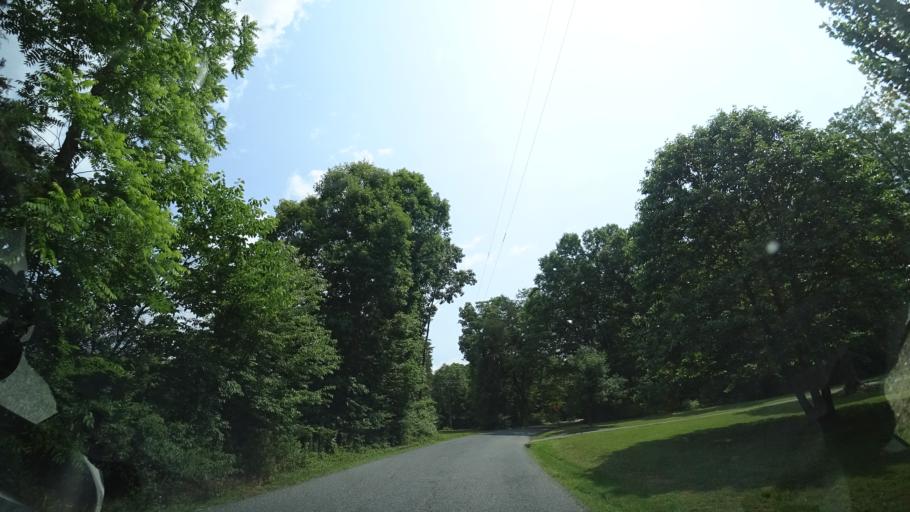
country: US
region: Virginia
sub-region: Spotsylvania County
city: Spotsylvania
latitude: 38.1305
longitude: -77.7859
